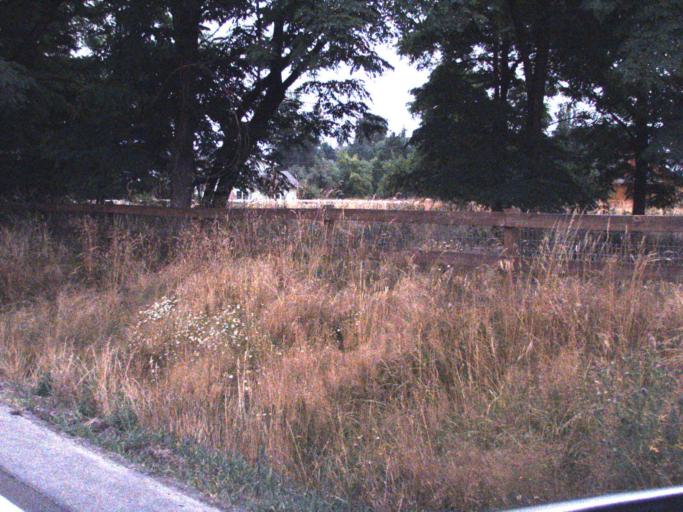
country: US
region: Washington
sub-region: King County
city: Carnation
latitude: 47.6285
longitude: -121.9113
